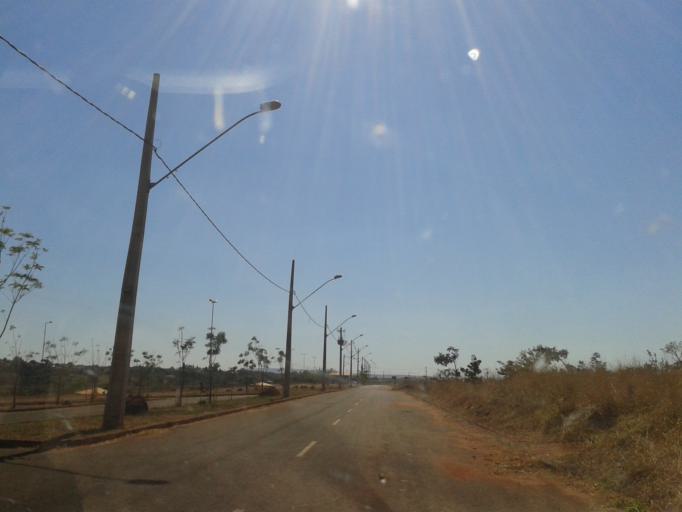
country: BR
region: Minas Gerais
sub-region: Ituiutaba
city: Ituiutaba
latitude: -19.0038
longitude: -49.4755
